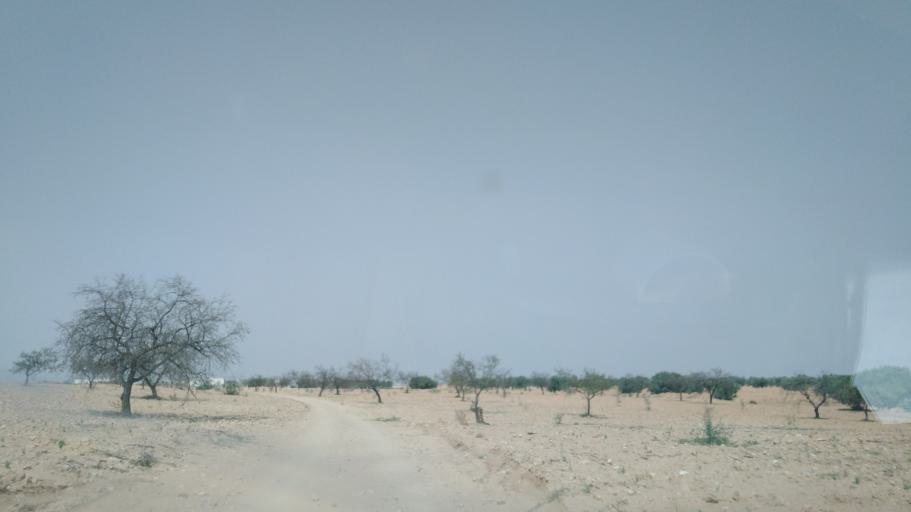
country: TN
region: Safaqis
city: Sfax
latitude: 34.6396
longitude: 10.5663
